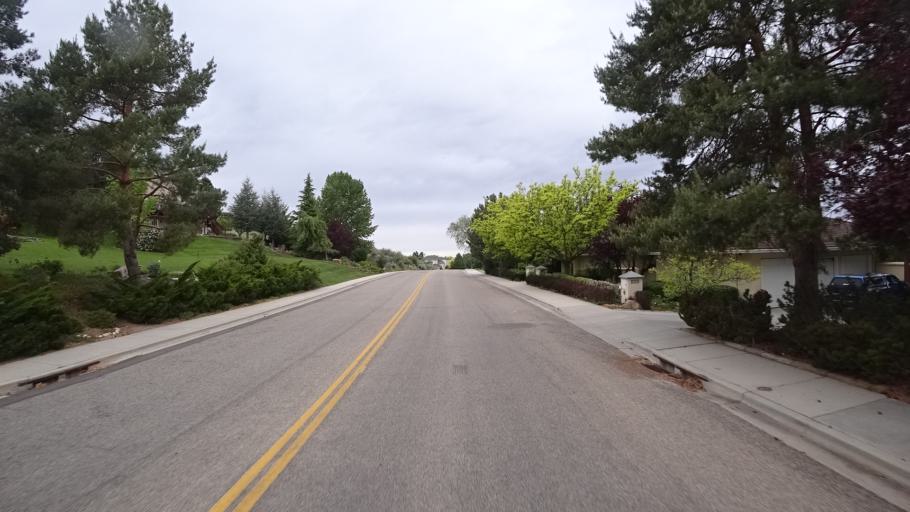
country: US
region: Idaho
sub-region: Ada County
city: Boise
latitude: 43.6133
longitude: -116.1577
